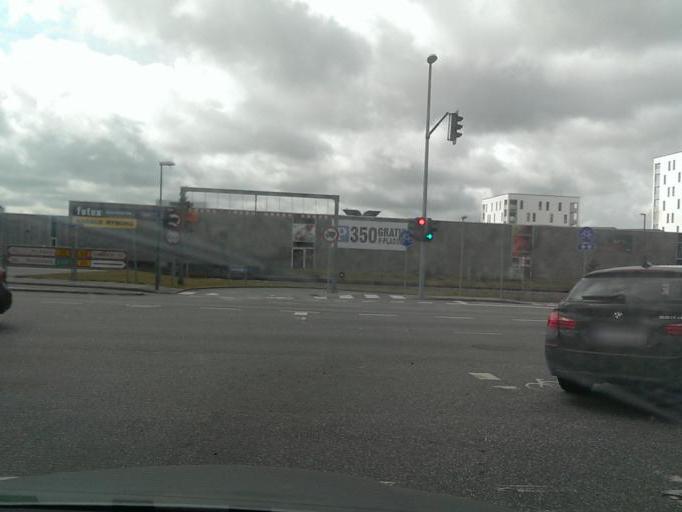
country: DK
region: North Denmark
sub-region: Hjorring Kommune
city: Hjorring
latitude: 57.4564
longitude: 9.9941
